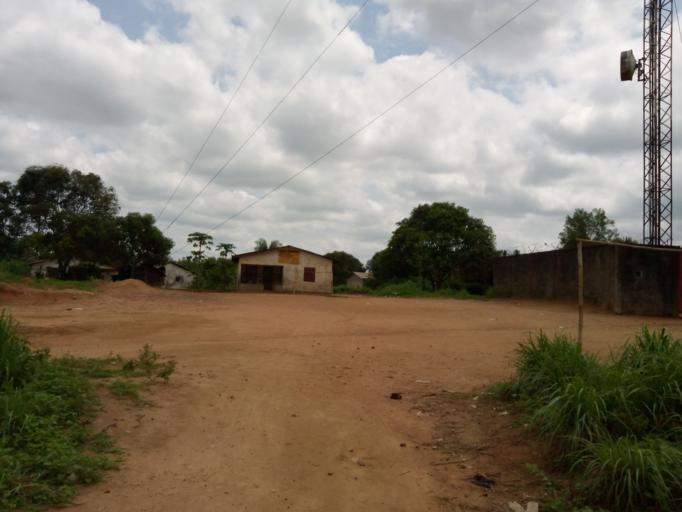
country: SL
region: Western Area
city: Waterloo
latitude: 8.3917
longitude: -12.9449
